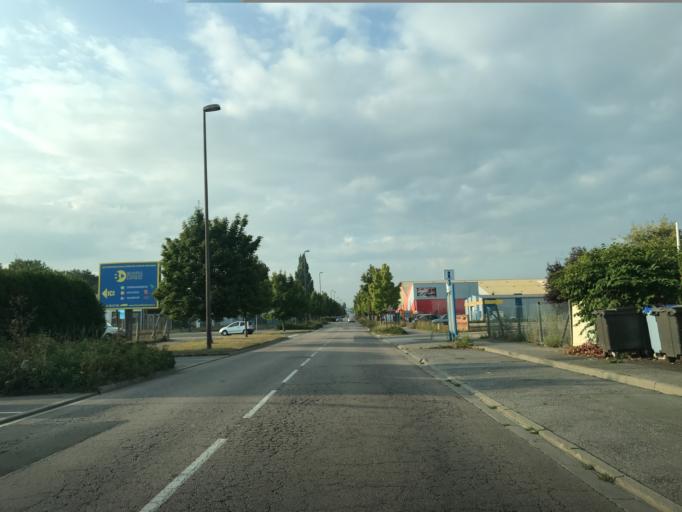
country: FR
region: Haute-Normandie
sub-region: Departement de l'Eure
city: Gravigny
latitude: 49.0279
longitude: 1.1848
